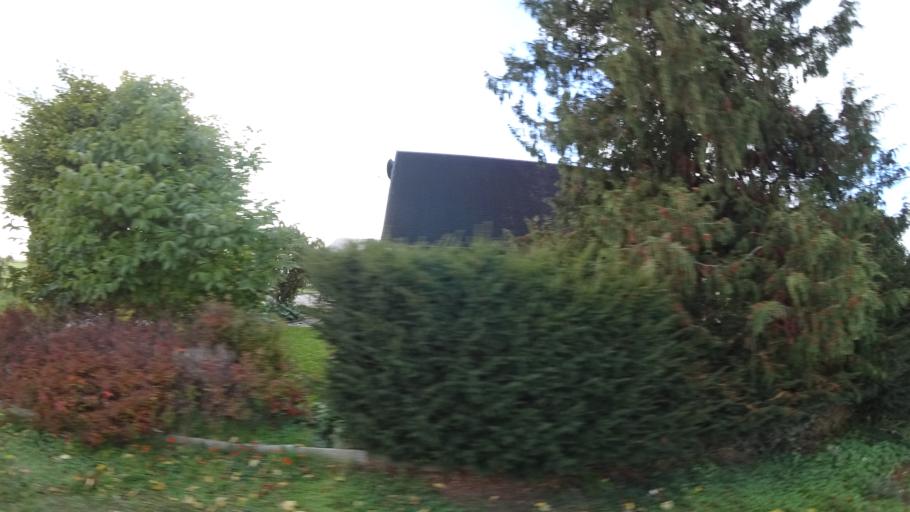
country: SE
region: Skane
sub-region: Staffanstorps Kommun
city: Staffanstorp
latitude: 55.6208
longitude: 13.2045
